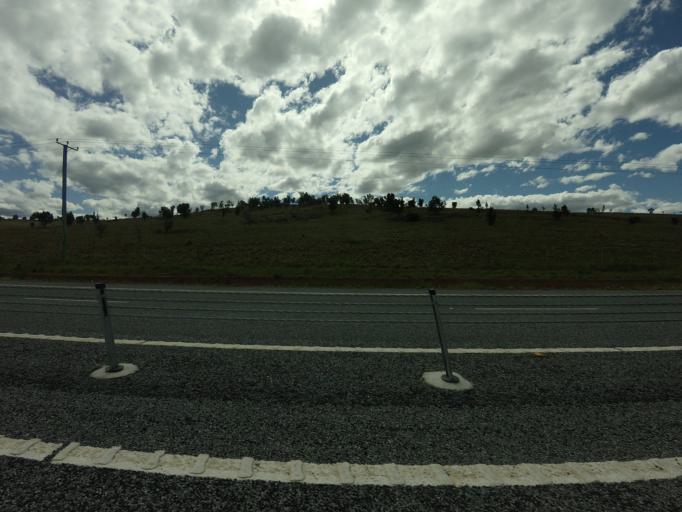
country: AU
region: Tasmania
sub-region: Northern Midlands
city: Evandale
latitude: -42.1209
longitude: 147.4375
